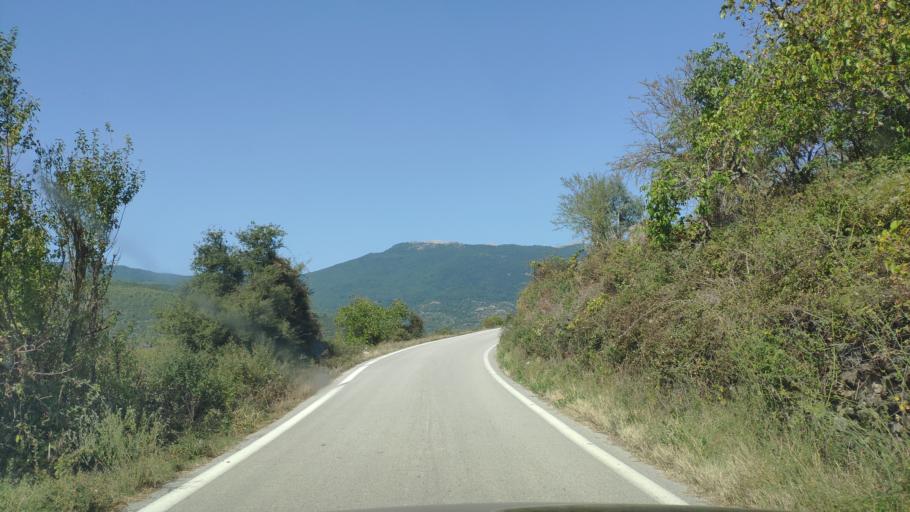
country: GR
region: West Greece
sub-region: Nomos Achaias
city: Aiyira
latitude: 37.9136
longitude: 22.3296
